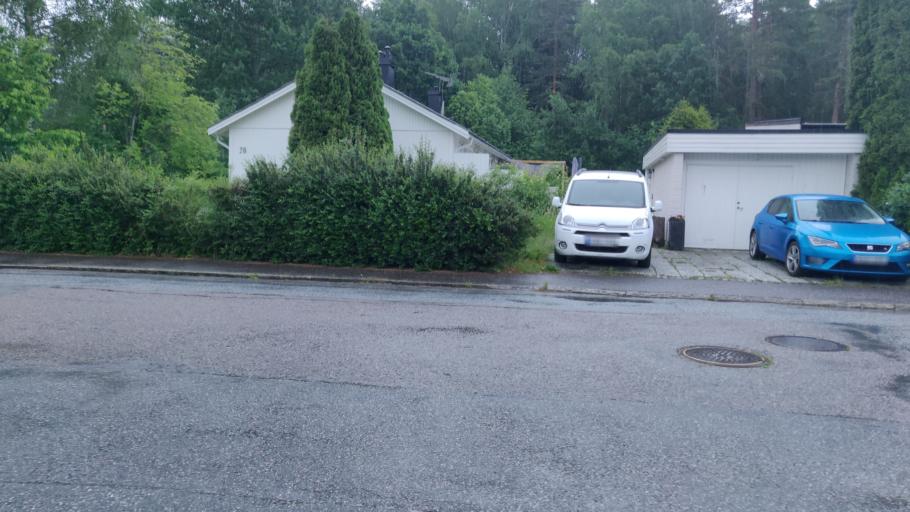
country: SE
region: OErebro
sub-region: Orebro Kommun
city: Orebro
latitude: 59.2978
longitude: 15.1719
